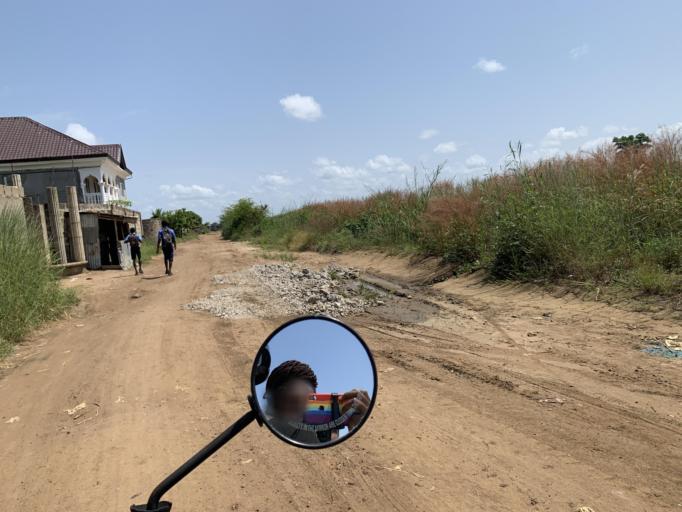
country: SL
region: Western Area
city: Hastings
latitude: 8.3953
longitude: -13.1276
